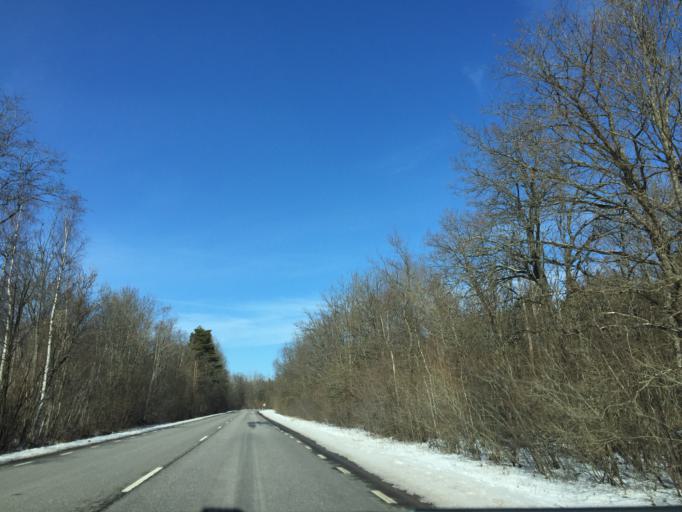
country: EE
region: Laeaene
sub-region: Lihula vald
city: Lihula
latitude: 58.6052
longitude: 23.6974
